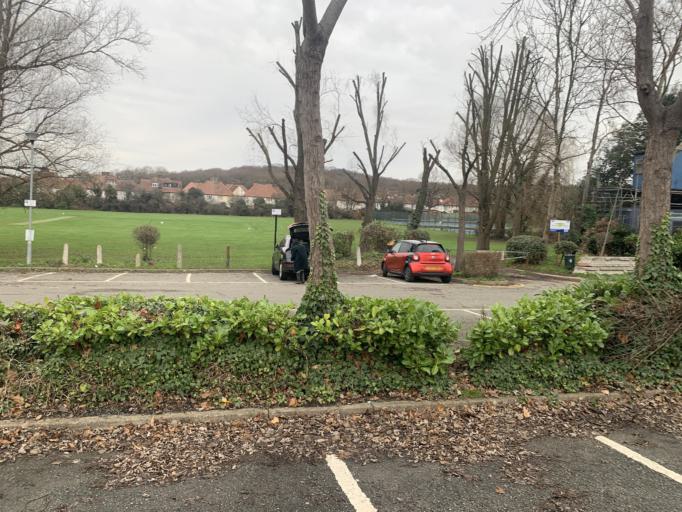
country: GB
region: England
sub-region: Greater London
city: Walthamstow
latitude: 51.6098
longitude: -0.0056
